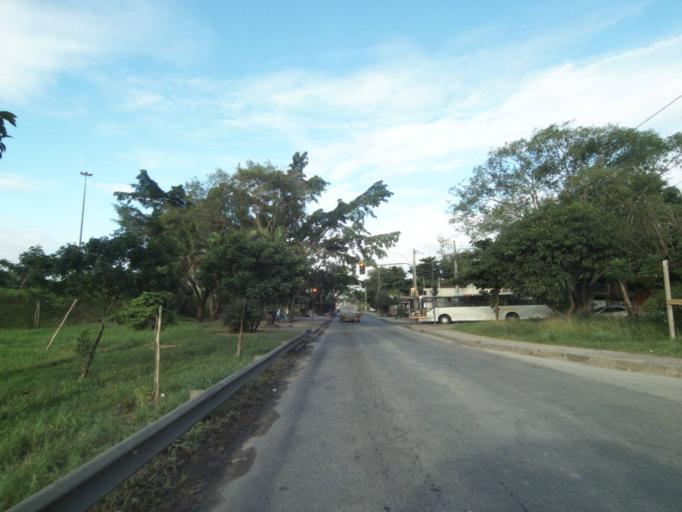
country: BR
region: Rio de Janeiro
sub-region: Nilopolis
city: Nilopolis
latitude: -22.8575
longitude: -43.4724
